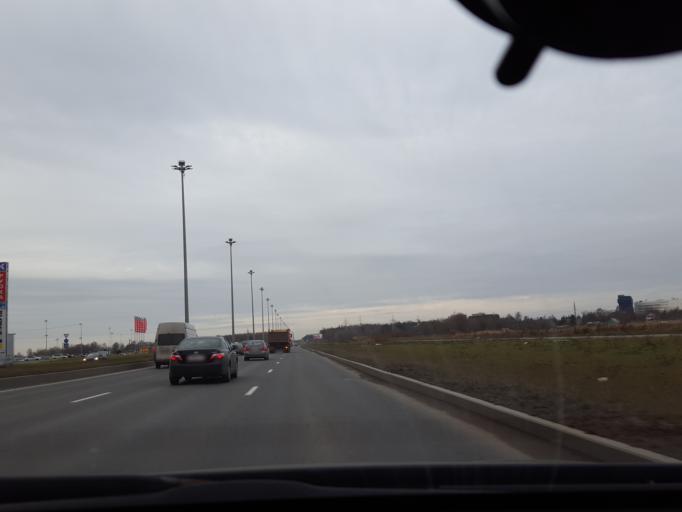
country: RU
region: St.-Petersburg
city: Kolomyagi
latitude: 60.0380
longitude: 30.2443
